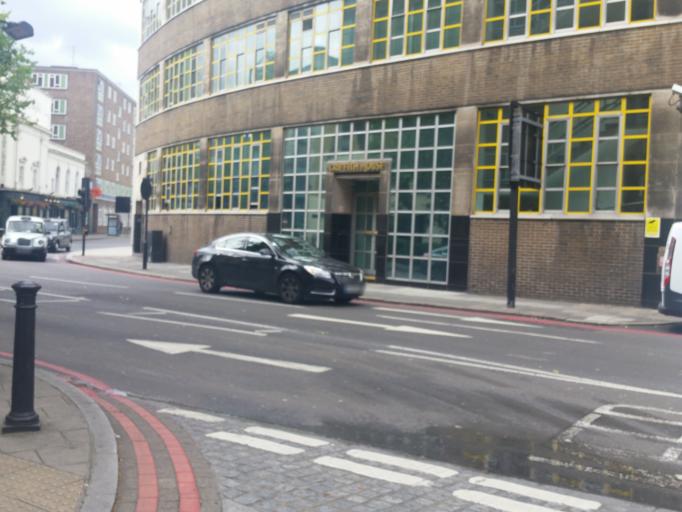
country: GB
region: England
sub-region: Greater London
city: Bayswater
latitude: 51.5204
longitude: -0.1655
